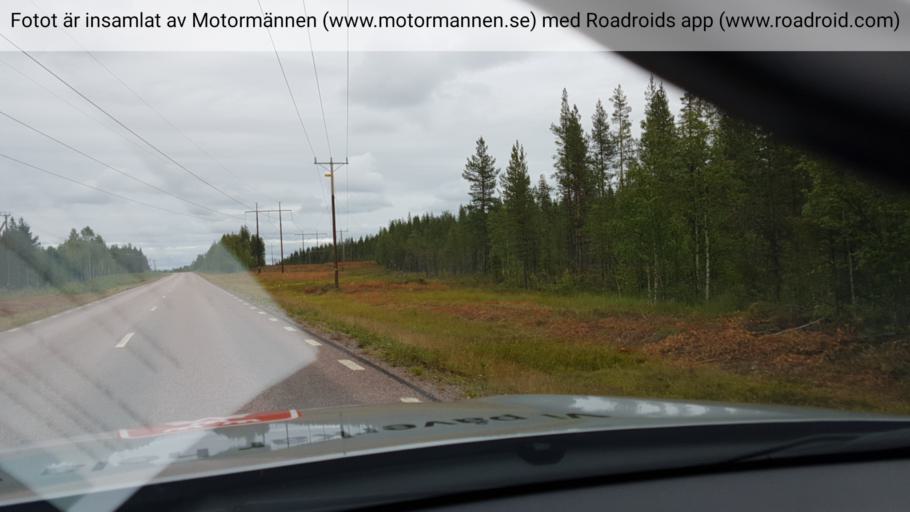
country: SE
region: Norrbotten
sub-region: Pajala Kommun
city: Pajala
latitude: 67.0936
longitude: 22.5711
